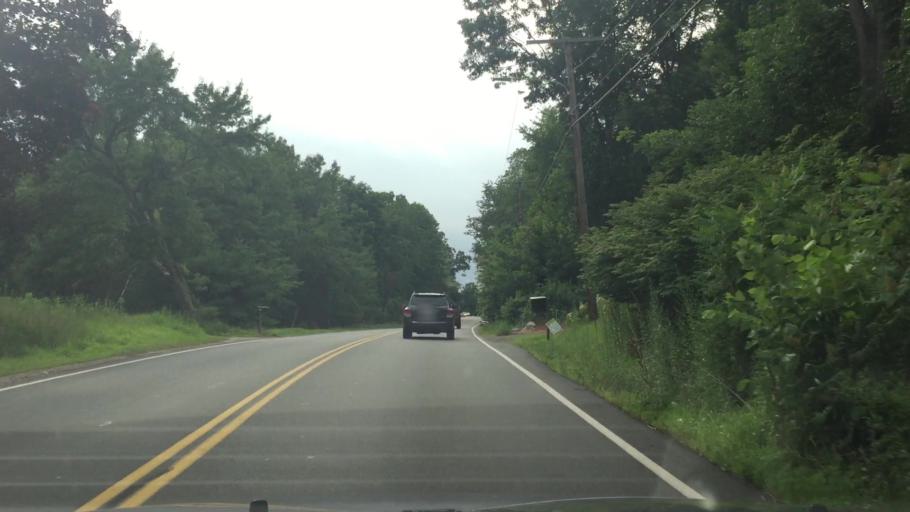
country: US
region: New Hampshire
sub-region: Rockingham County
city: Salem
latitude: 42.7884
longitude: -71.1742
